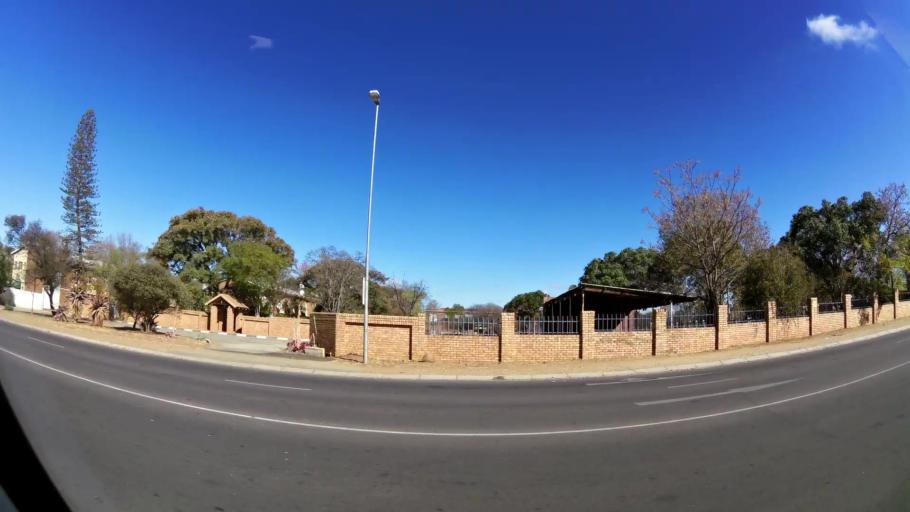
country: ZA
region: Limpopo
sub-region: Capricorn District Municipality
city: Polokwane
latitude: -23.9079
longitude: 29.4739
